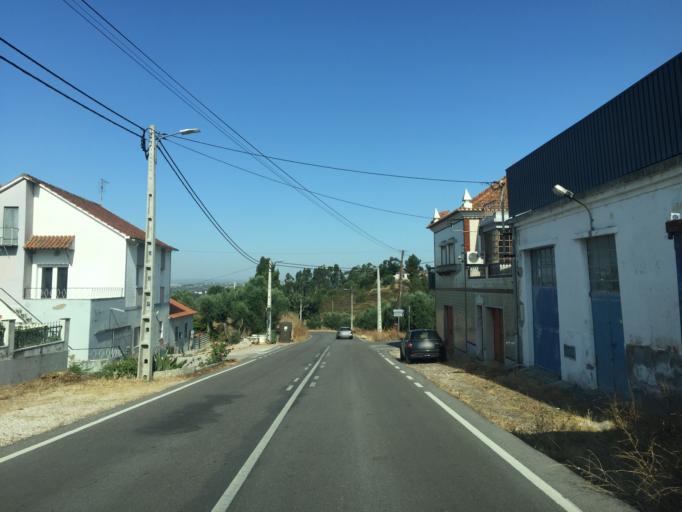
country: PT
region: Santarem
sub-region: Tomar
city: Tomar
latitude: 39.5909
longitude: -8.3510
